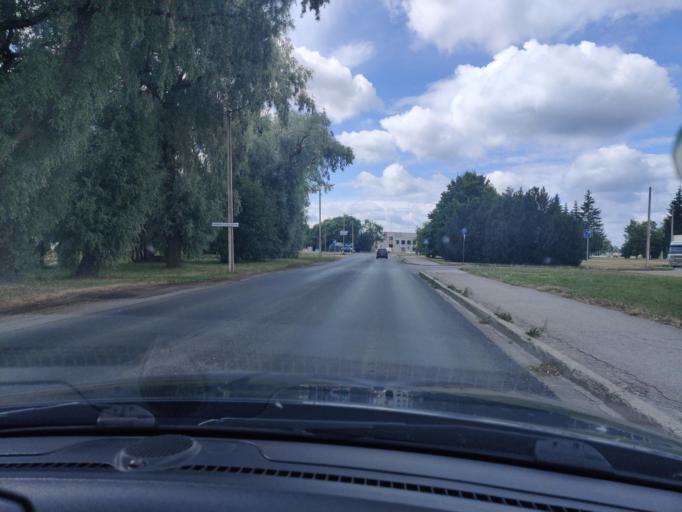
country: EE
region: Harju
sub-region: Tallinna linn
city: Tallinn
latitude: 59.4182
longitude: 24.6816
